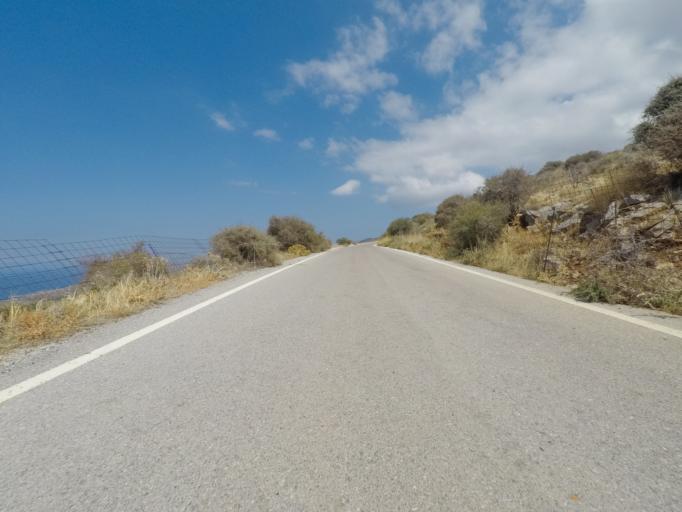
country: GR
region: Crete
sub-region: Nomos Lasithiou
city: Elounda
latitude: 35.3184
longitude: 25.6742
